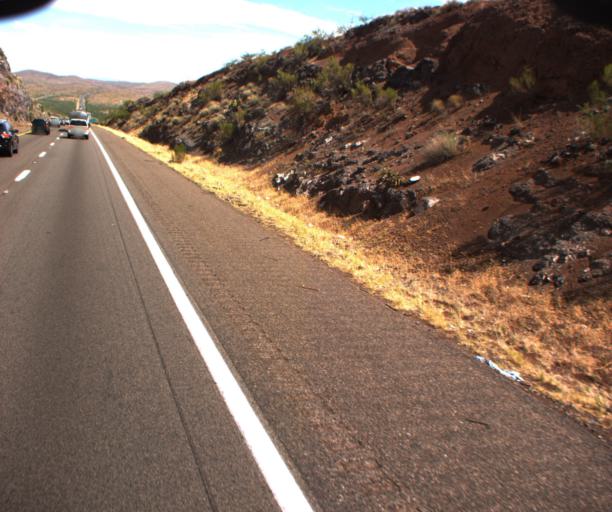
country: US
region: Arizona
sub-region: Yavapai County
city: Cordes Lakes
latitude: 34.2266
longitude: -112.1109
